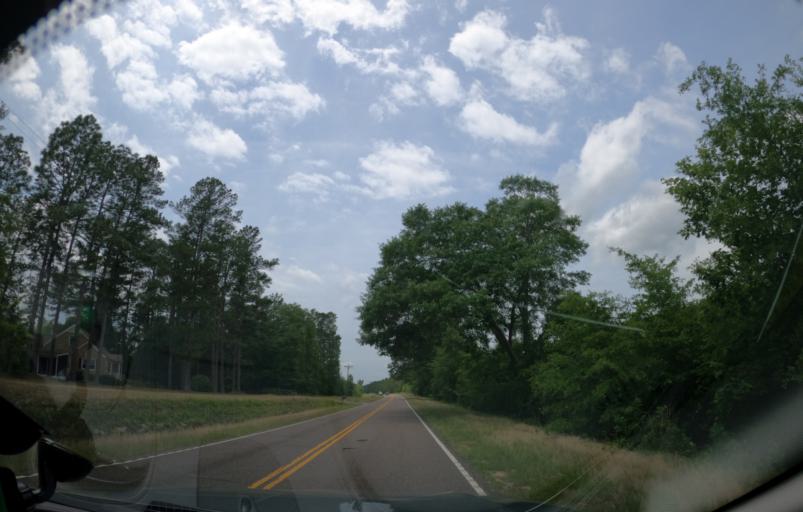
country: US
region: South Carolina
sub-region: Barnwell County
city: Williston
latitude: 33.5758
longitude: -81.4385
